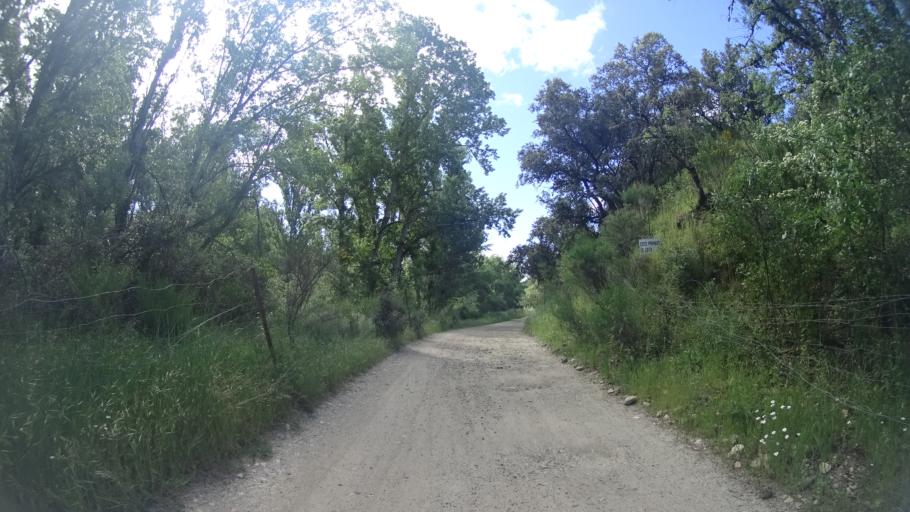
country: ES
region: Madrid
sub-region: Provincia de Madrid
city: Brunete
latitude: 40.4257
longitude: -3.9526
